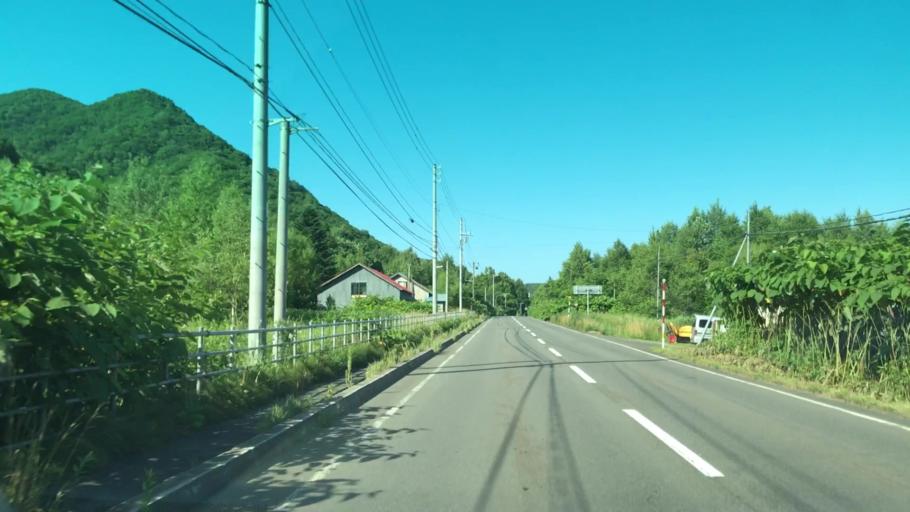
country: JP
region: Hokkaido
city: Yoichi
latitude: 43.0568
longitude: 140.8647
